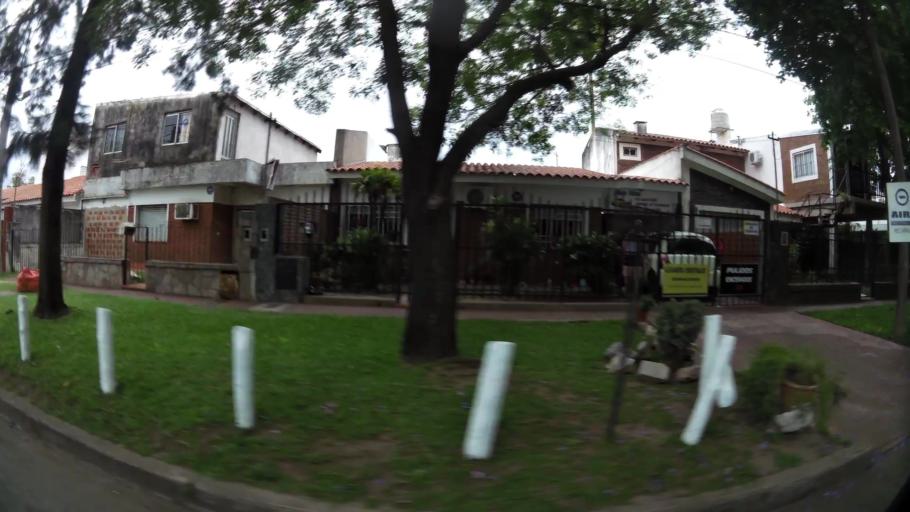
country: AR
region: Santa Fe
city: Granadero Baigorria
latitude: -32.8730
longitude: -60.6971
